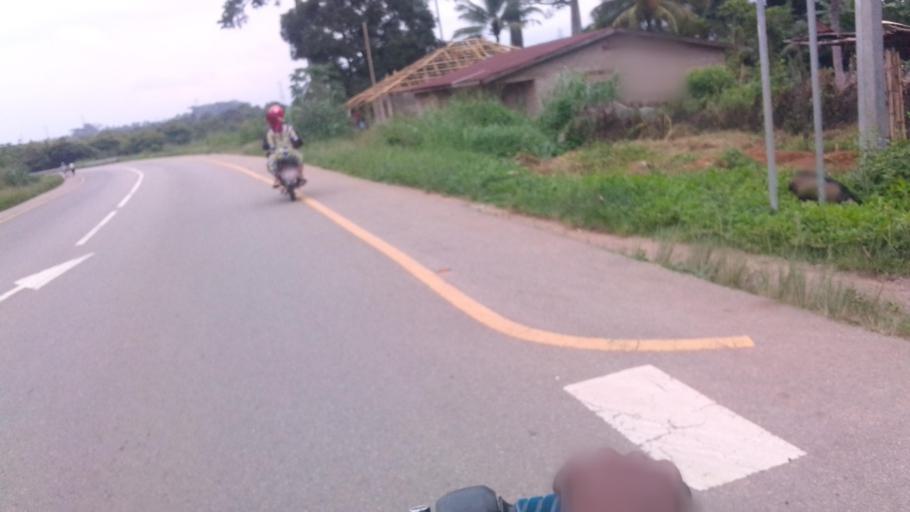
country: SL
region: Eastern Province
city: Hangha
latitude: 7.9406
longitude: -11.1402
